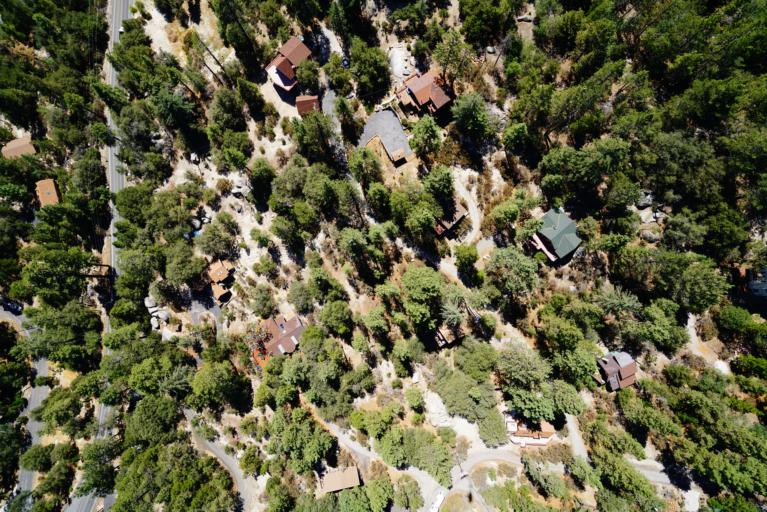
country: US
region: California
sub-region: Riverside County
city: Idyllwild-Pine Cove
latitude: 33.7534
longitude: -116.7269
